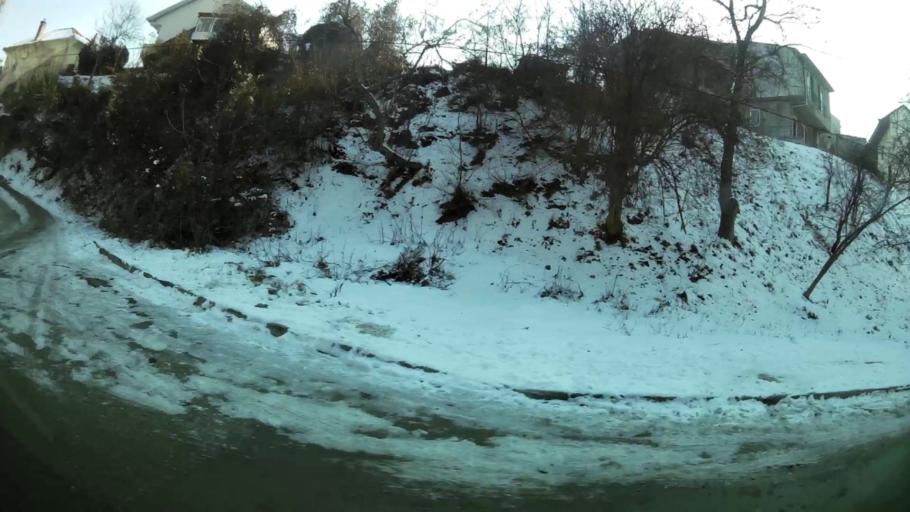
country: MK
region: Kisela Voda
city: Usje
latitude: 41.9659
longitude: 21.4461
